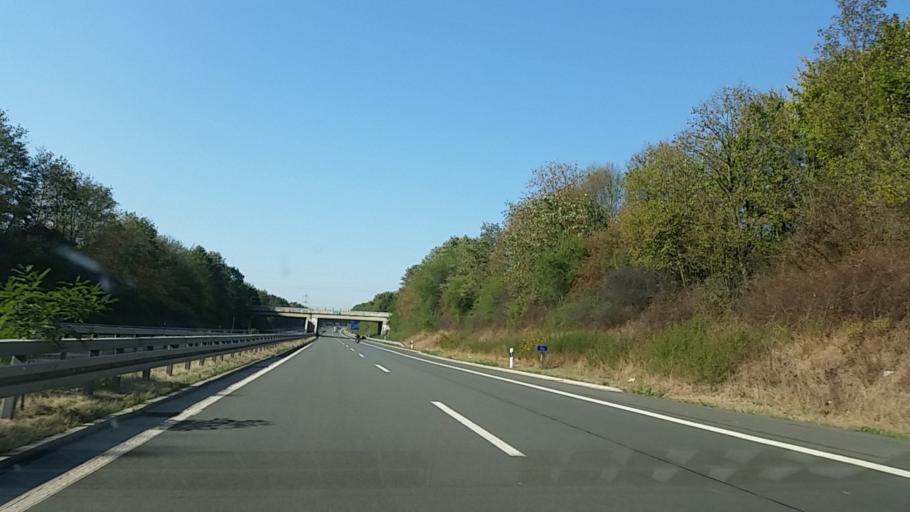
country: DE
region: North Rhine-Westphalia
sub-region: Regierungsbezirk Dusseldorf
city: Langenfeld
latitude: 51.0912
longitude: 6.9482
